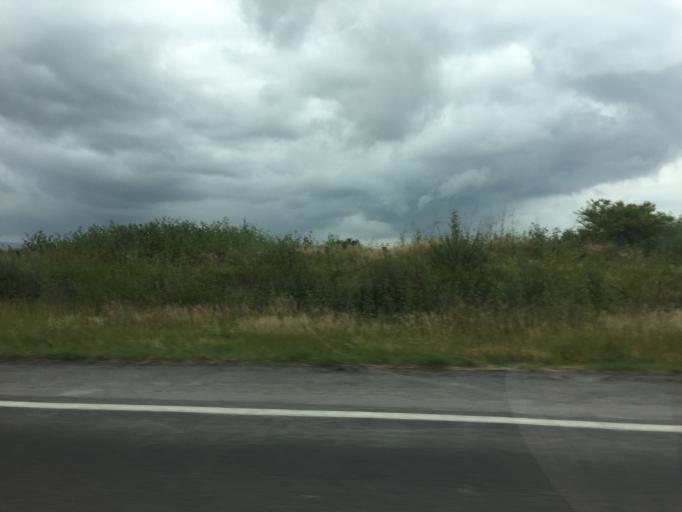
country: MX
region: Jalisco
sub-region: Zapotlanejo
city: La Mezquitera
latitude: 20.5732
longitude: -103.0857
